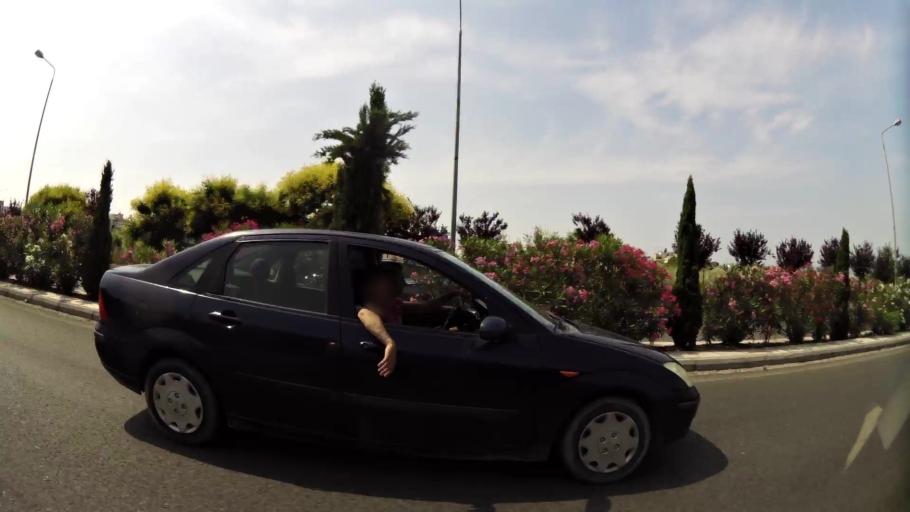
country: GR
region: Central Macedonia
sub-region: Nomos Thessalonikis
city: Triandria
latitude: 40.6260
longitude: 22.9728
